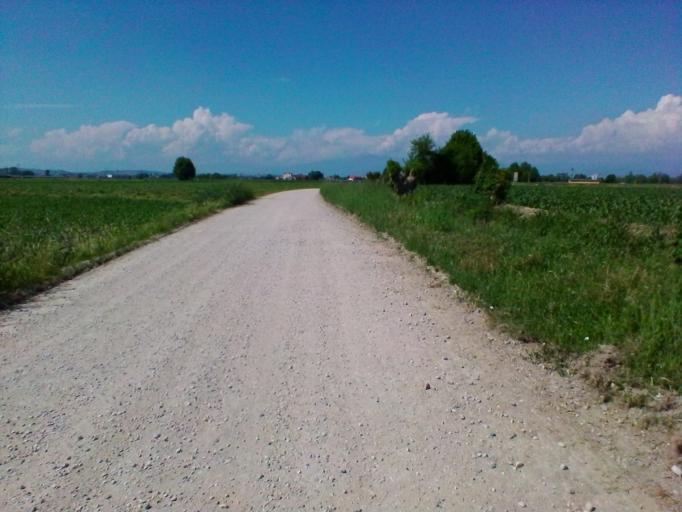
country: IT
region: Veneto
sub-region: Provincia di Verona
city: Povegliano Veronese
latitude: 45.3290
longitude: 10.8768
